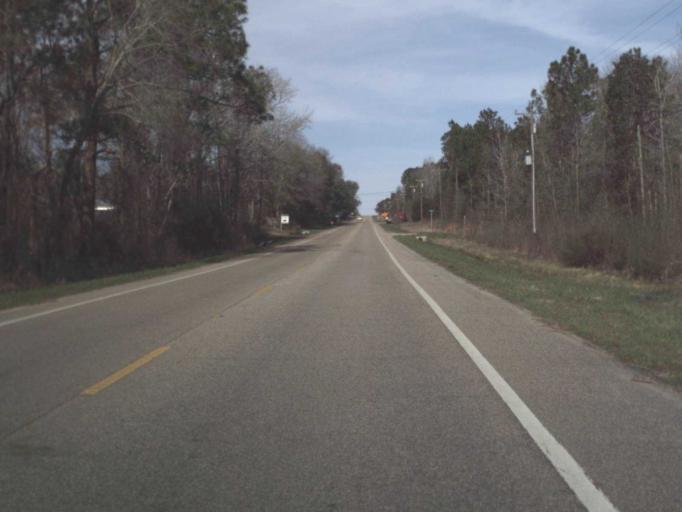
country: US
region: Florida
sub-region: Washington County
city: Chipley
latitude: 30.8580
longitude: -85.5280
